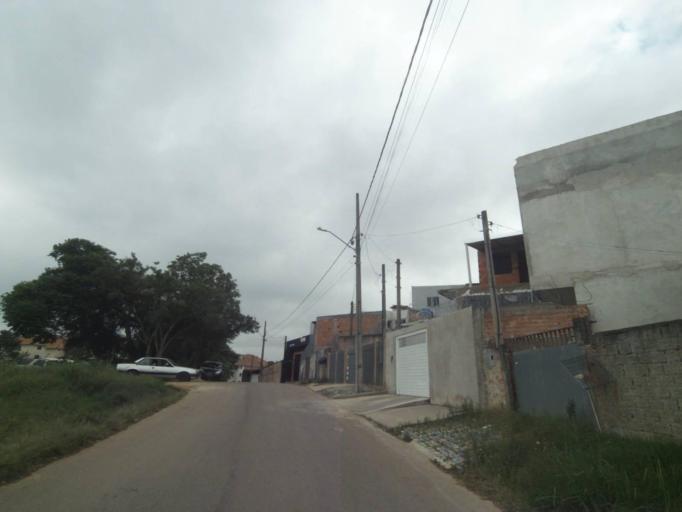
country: BR
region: Parana
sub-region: Curitiba
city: Curitiba
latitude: -25.4811
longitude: -49.3556
